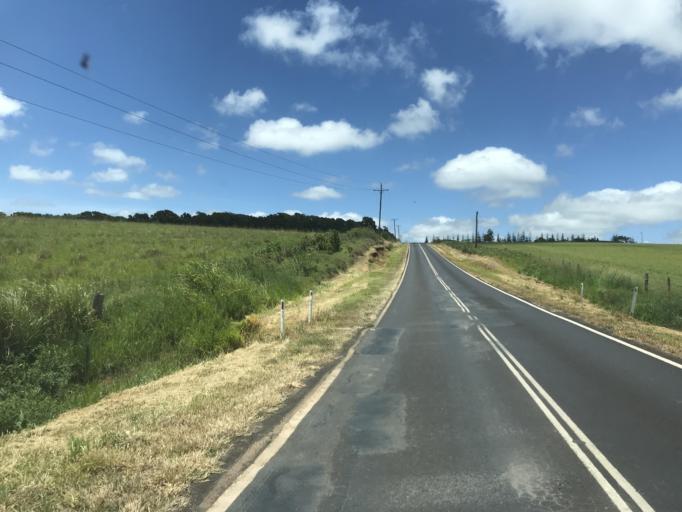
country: AU
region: Queensland
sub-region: Tablelands
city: Ravenshoe
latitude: -17.5051
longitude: 145.4763
